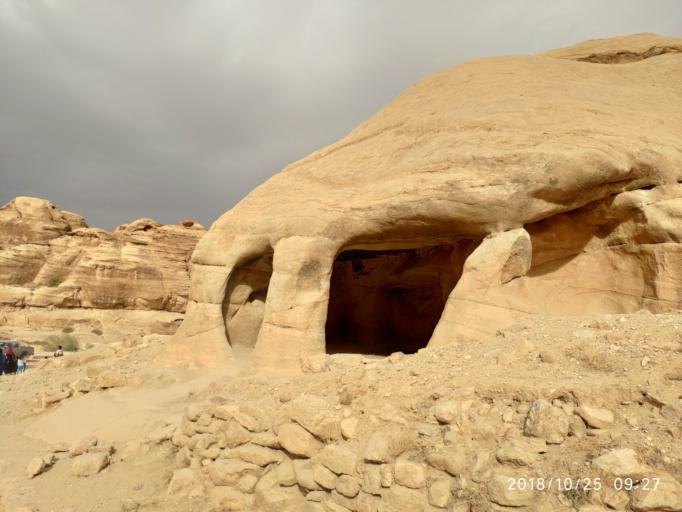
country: JO
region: Ma'an
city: Petra
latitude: 30.3210
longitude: 35.4624
